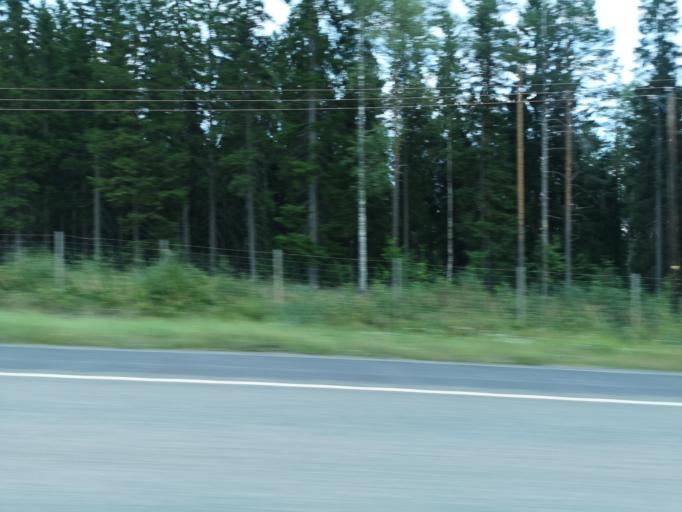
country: FI
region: Central Finland
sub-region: Joutsa
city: Joutsa
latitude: 61.8165
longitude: 26.0945
